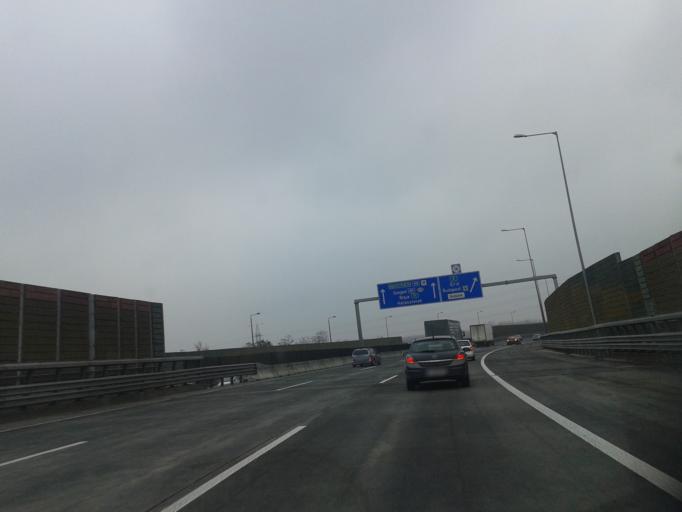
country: HU
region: Budapest
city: Budapest XXII. keruelet
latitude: 47.4004
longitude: 19.0067
